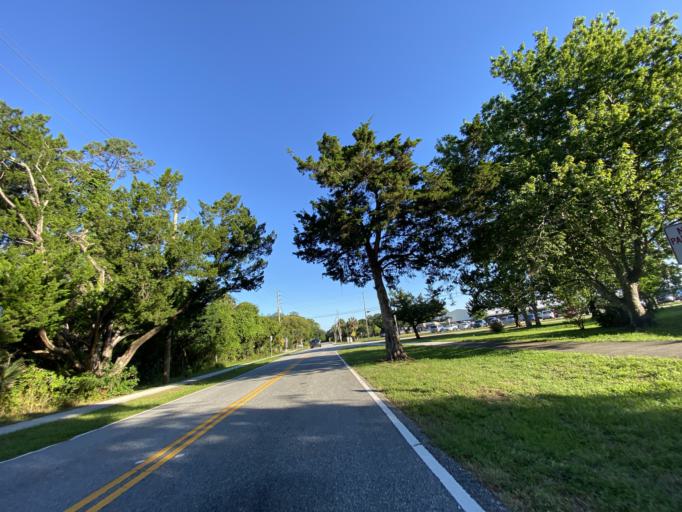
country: US
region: Florida
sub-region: Volusia County
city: Port Orange
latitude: 29.1459
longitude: -81.0012
